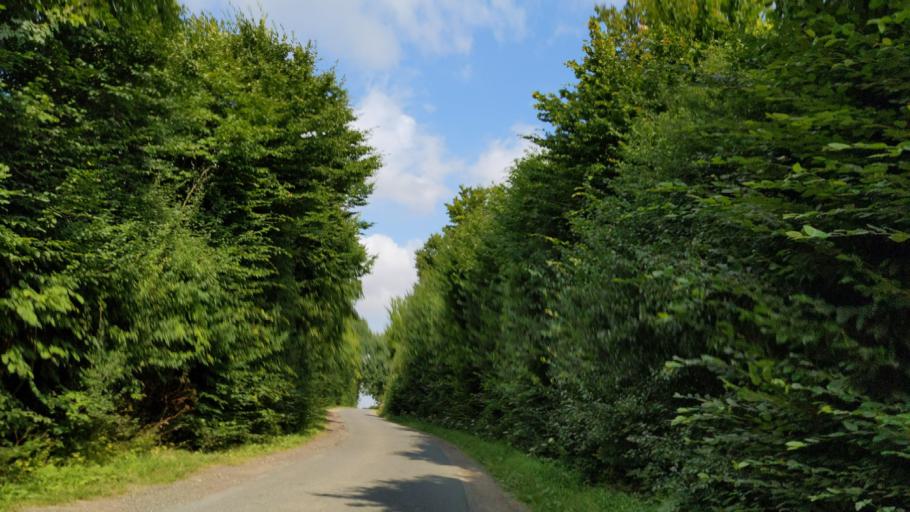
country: DE
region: Schleswig-Holstein
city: Badendorf
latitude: 53.8995
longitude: 10.5990
